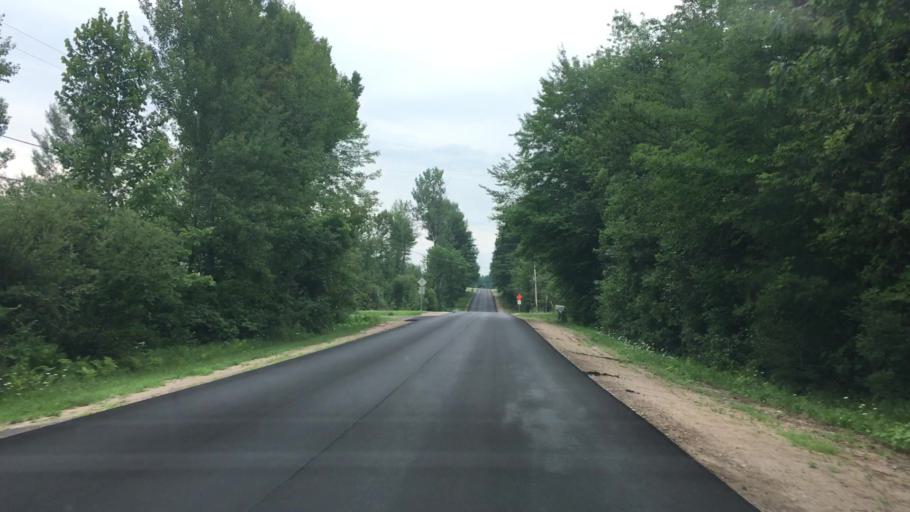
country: US
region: New York
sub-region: Clinton County
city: Peru
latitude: 44.5769
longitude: -73.5699
